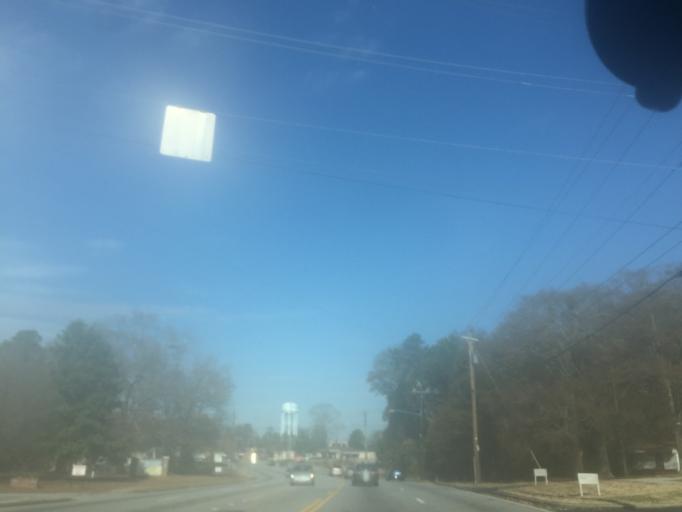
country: US
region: Georgia
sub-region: Clayton County
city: Riverdale
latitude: 33.5733
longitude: -84.4153
